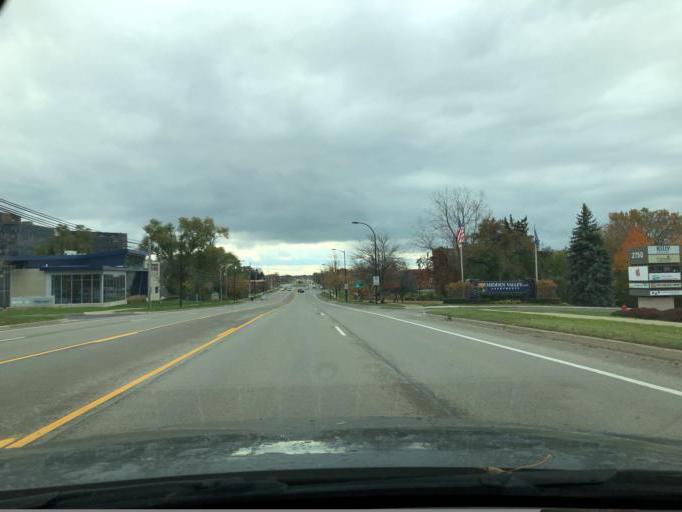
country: US
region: Michigan
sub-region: Washtenaw County
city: Ann Arbor
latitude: 42.2477
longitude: -83.7394
